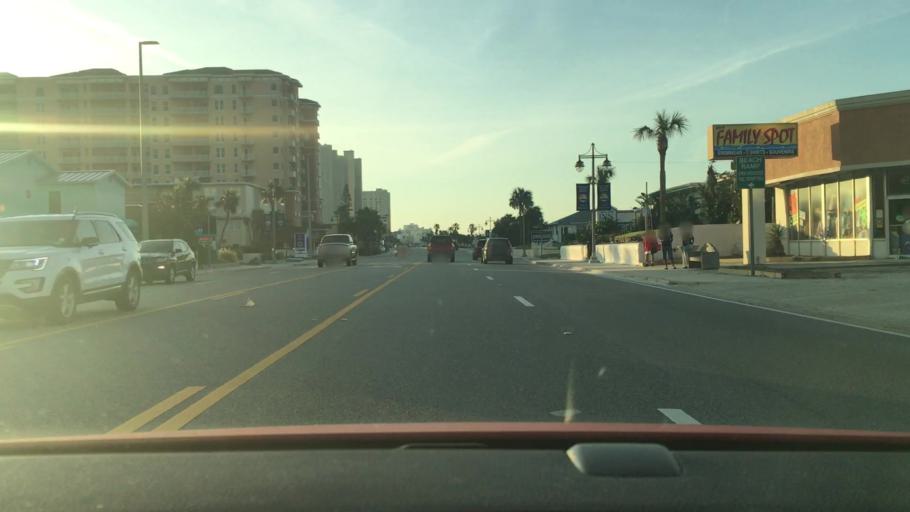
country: US
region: Florida
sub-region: Volusia County
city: Daytona Beach Shores
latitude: 29.1592
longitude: -80.9738
